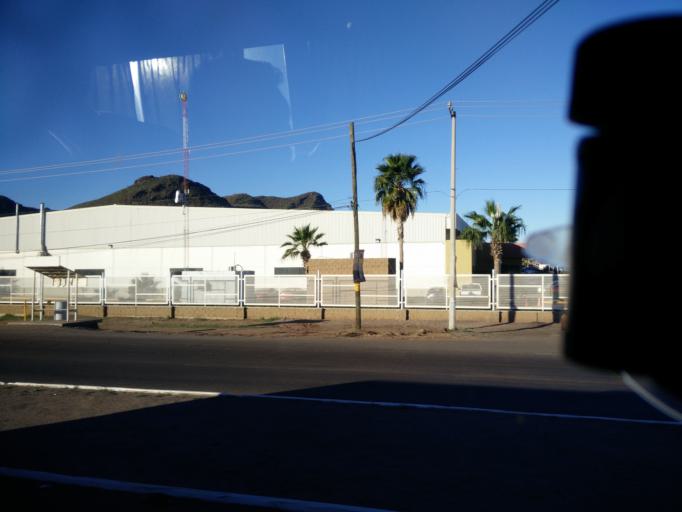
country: MX
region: Sonora
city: Heroica Guaymas
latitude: 27.9591
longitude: -110.9354
